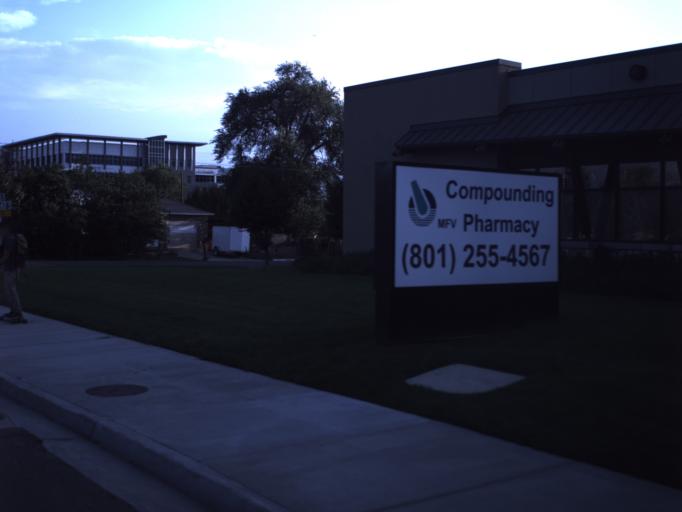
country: US
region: Utah
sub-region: Salt Lake County
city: Sandy City
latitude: 40.5781
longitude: -111.8910
